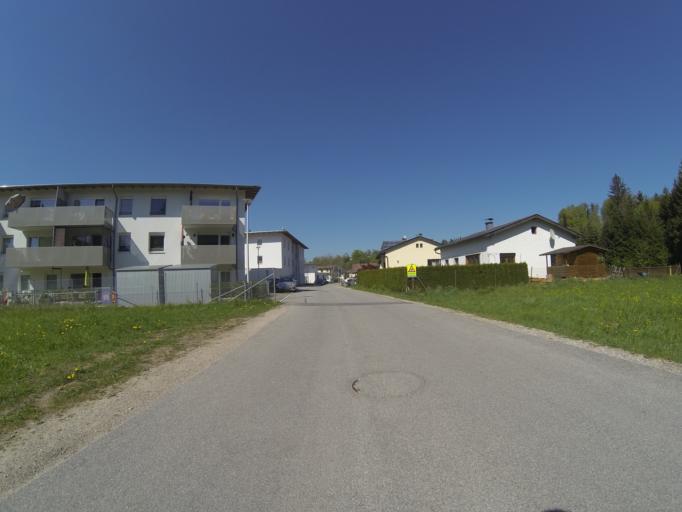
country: AT
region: Upper Austria
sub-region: Politischer Bezirk Gmunden
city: Altmunster
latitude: 47.9454
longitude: 13.7517
